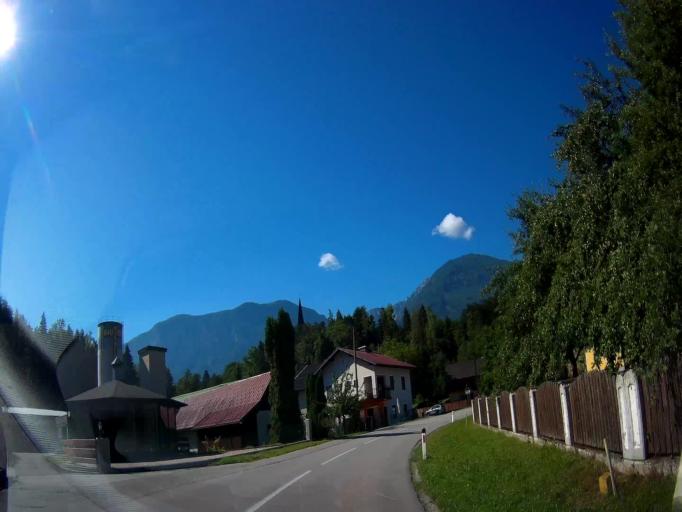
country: AT
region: Carinthia
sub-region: Politischer Bezirk Volkermarkt
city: Gallizien
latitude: 46.5624
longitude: 14.5059
